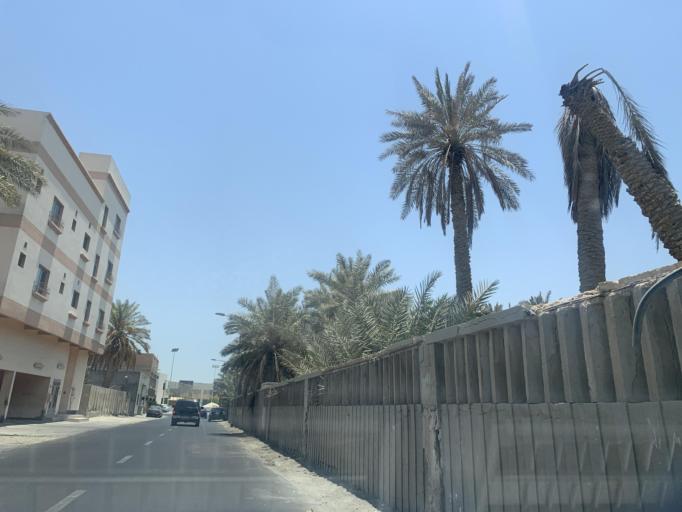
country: BH
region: Muharraq
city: Al Muharraq
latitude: 26.2834
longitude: 50.6201
